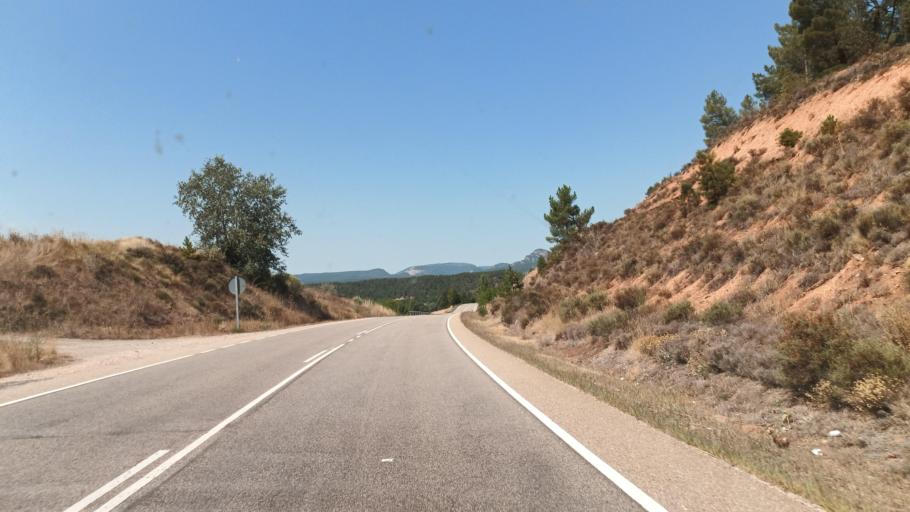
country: ES
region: Castille and Leon
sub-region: Provincia de Burgos
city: Salas de Bureba
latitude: 42.6735
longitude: -3.4192
